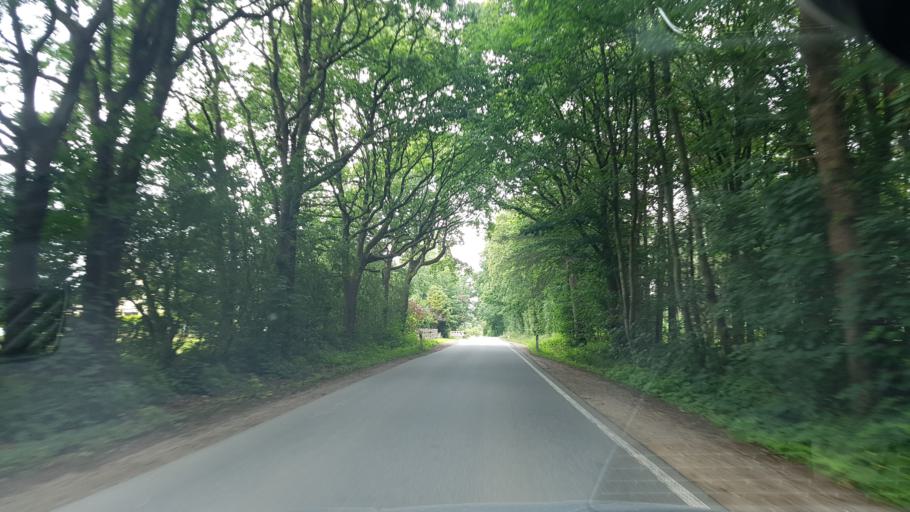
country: DE
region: Schleswig-Holstein
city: Wallsbull
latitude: 54.7828
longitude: 9.2436
